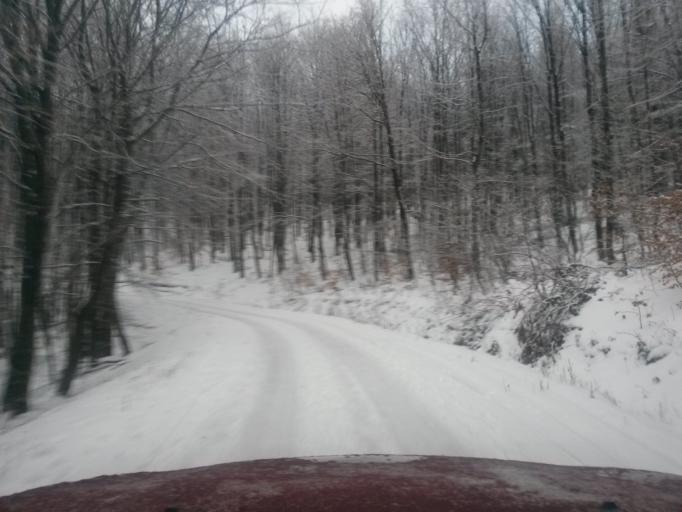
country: SK
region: Kosicky
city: Kosice
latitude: 48.7631
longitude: 21.1262
